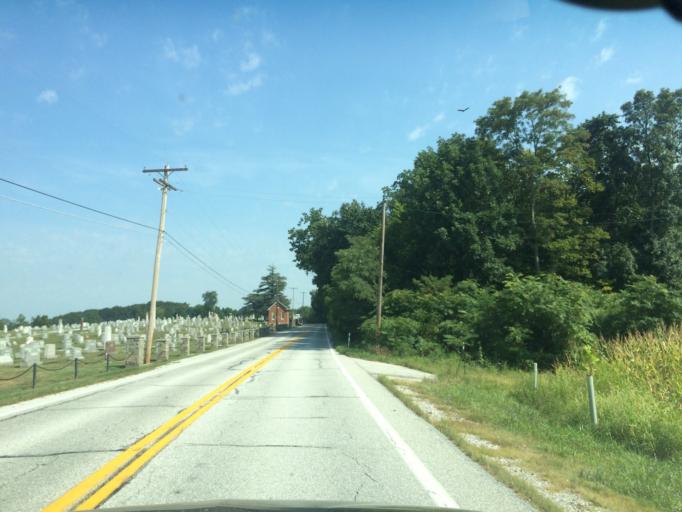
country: US
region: Maryland
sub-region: Carroll County
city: New Windsor
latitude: 39.5738
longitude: -77.1262
